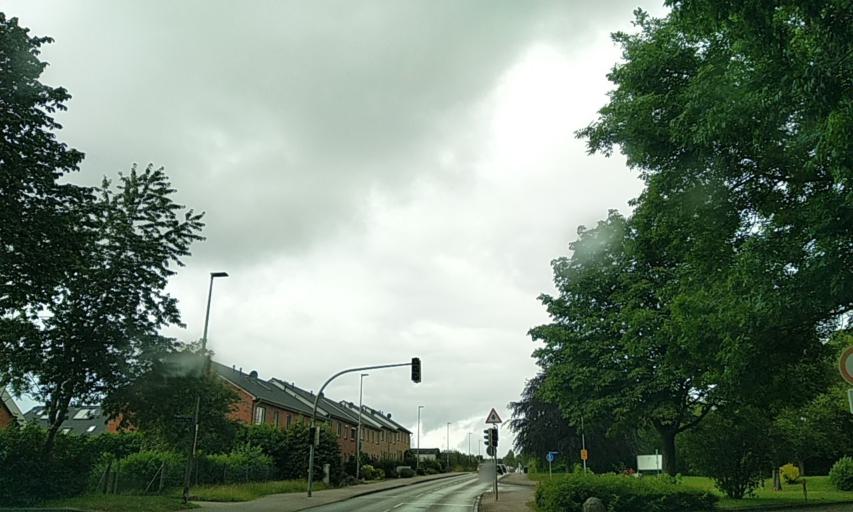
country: DE
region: Schleswig-Holstein
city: Schleswig
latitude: 54.5293
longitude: 9.5574
